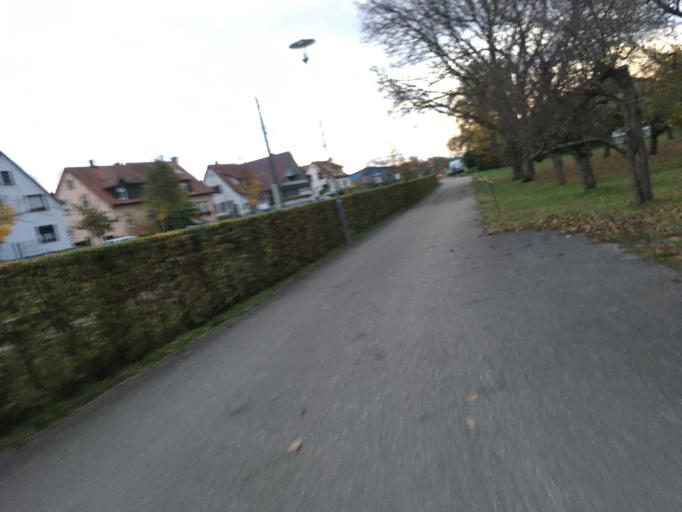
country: DE
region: Baden-Wuerttemberg
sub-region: Freiburg Region
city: Bahlingen
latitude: 48.1252
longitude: 7.7419
